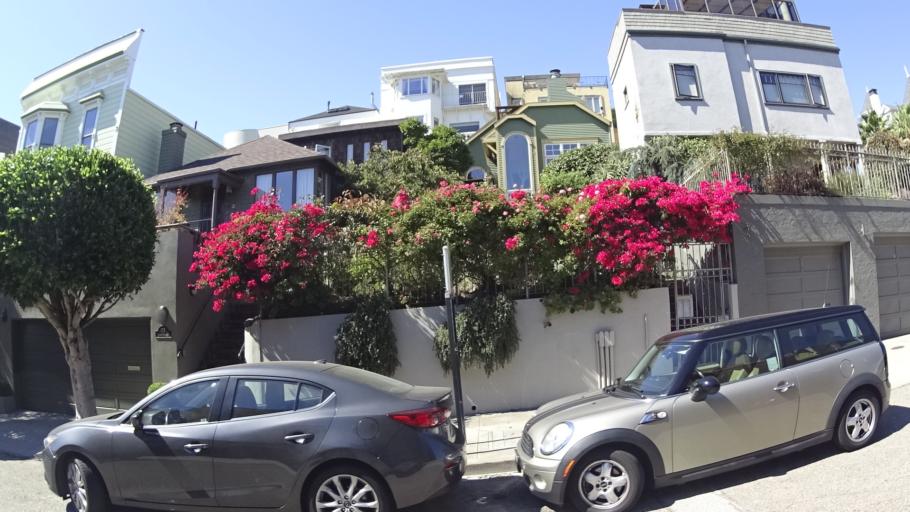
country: US
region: California
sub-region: San Francisco County
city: San Francisco
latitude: 37.7688
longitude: -122.4375
